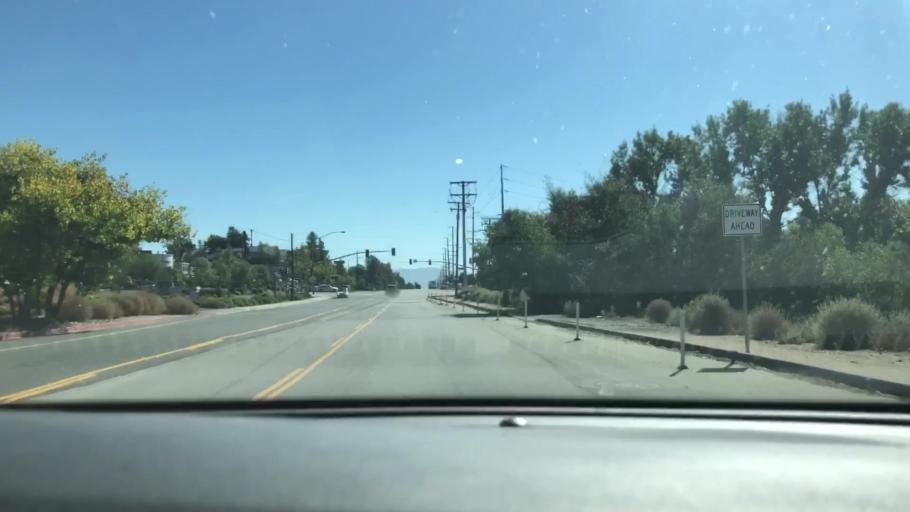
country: US
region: California
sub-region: Riverside County
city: Wildomar
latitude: 33.5902
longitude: -117.2535
